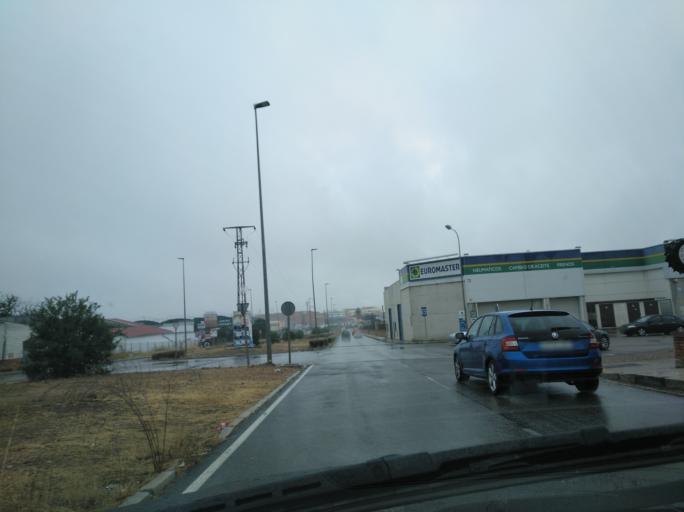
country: ES
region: Extremadura
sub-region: Provincia de Badajoz
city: Badajoz
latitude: 38.8941
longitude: -6.9922
